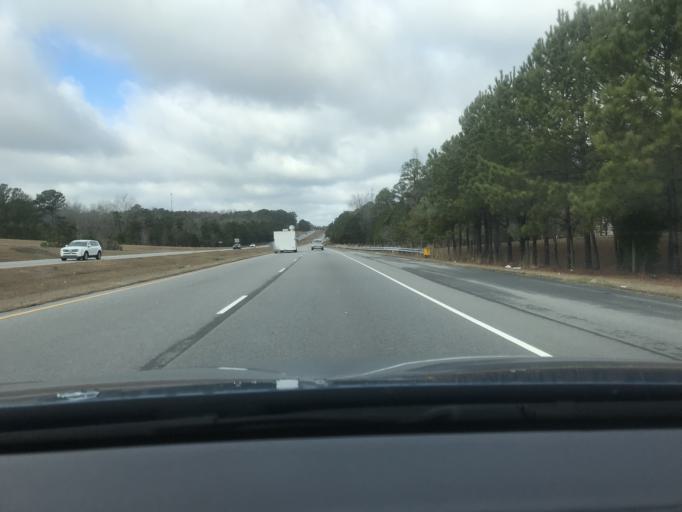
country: US
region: North Carolina
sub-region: Cumberland County
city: Spring Lake
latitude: 35.2702
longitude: -79.0606
